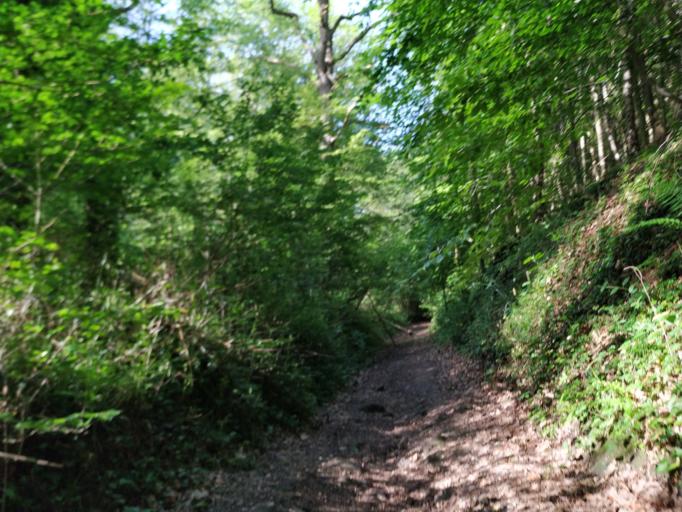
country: BE
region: Wallonia
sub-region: Province de Namur
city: Namur
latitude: 50.4800
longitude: 4.9292
